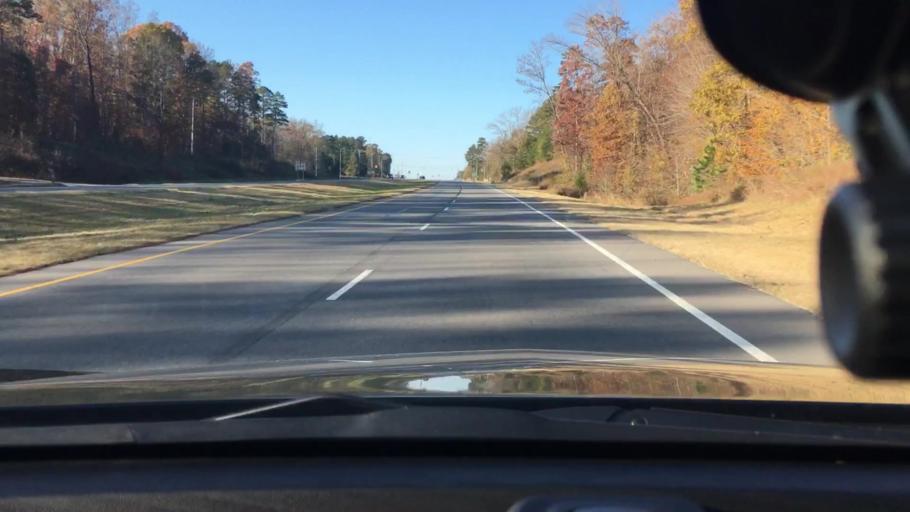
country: US
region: North Carolina
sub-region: Cabarrus County
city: Mount Pleasant
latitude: 35.3968
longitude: -80.4768
